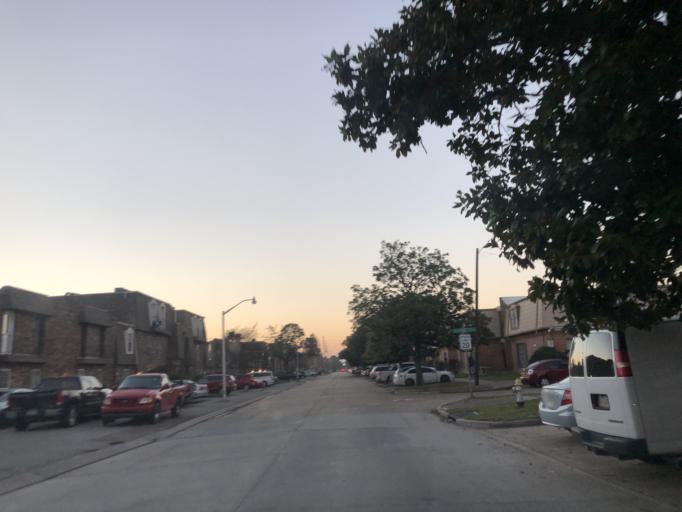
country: US
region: Louisiana
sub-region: Jefferson Parish
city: Kenner
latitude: 30.0091
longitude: -90.2128
